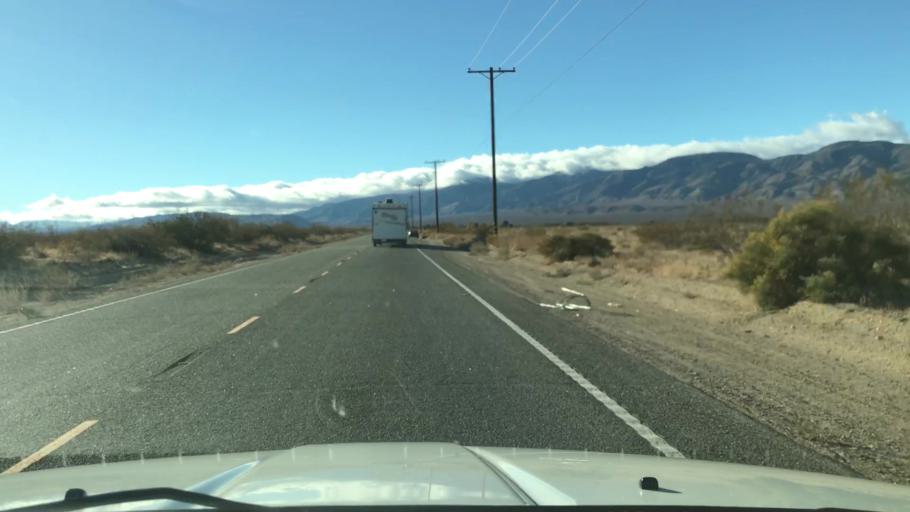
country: US
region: California
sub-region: Kern County
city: Mojave
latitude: 35.1255
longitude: -118.0947
